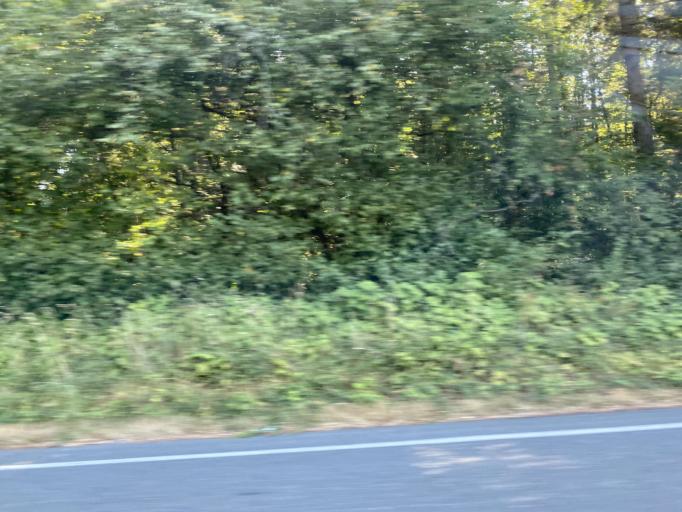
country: US
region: Washington
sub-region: Thurston County
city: Tanglewilde-Thompson Place
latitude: 46.9727
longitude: -122.7636
